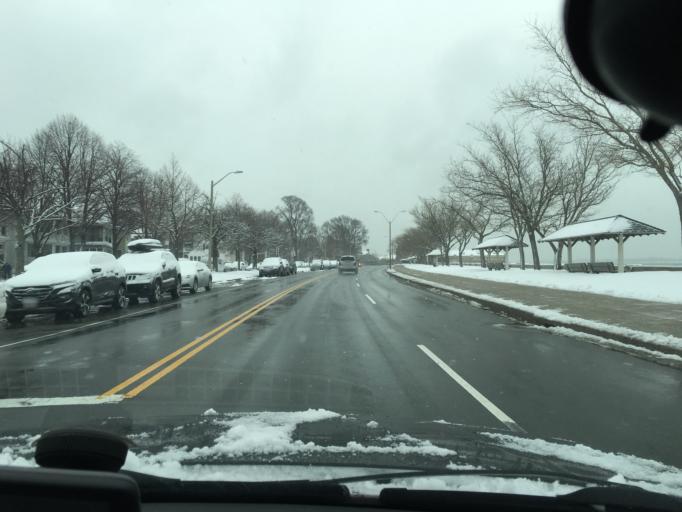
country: US
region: Massachusetts
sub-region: Suffolk County
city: South Boston
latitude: 42.3301
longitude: -71.0398
